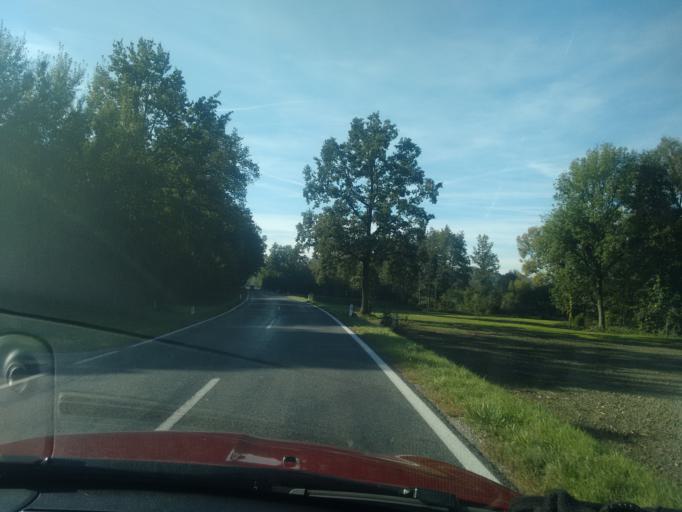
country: AT
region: Upper Austria
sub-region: Politischer Bezirk Vocklabruck
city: Manning
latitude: 48.0784
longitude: 13.6641
